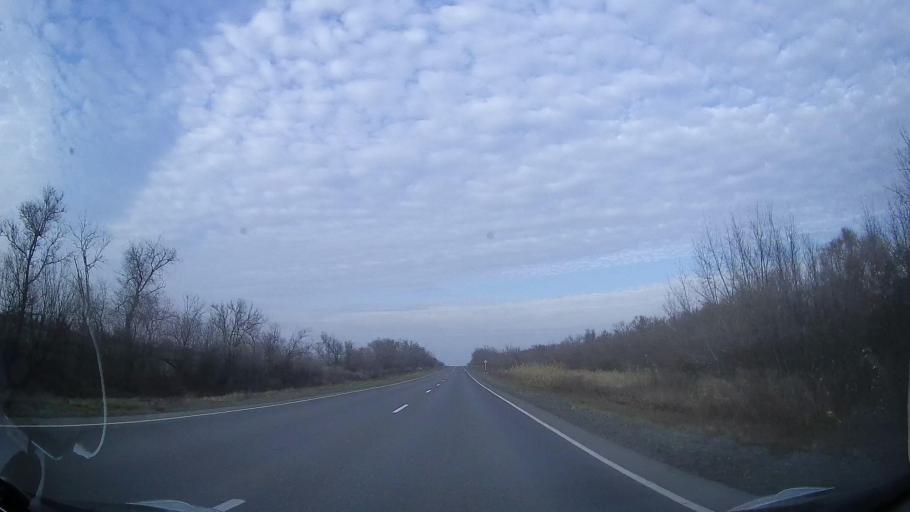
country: RU
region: Rostov
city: Bagayevskaya
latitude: 47.1424
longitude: 40.2766
